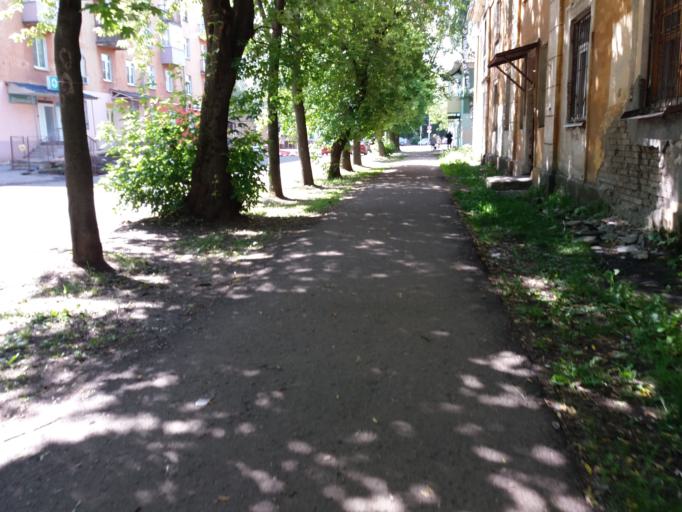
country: RU
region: Jaroslavl
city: Yaroslavl
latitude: 57.6385
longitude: 39.8396
